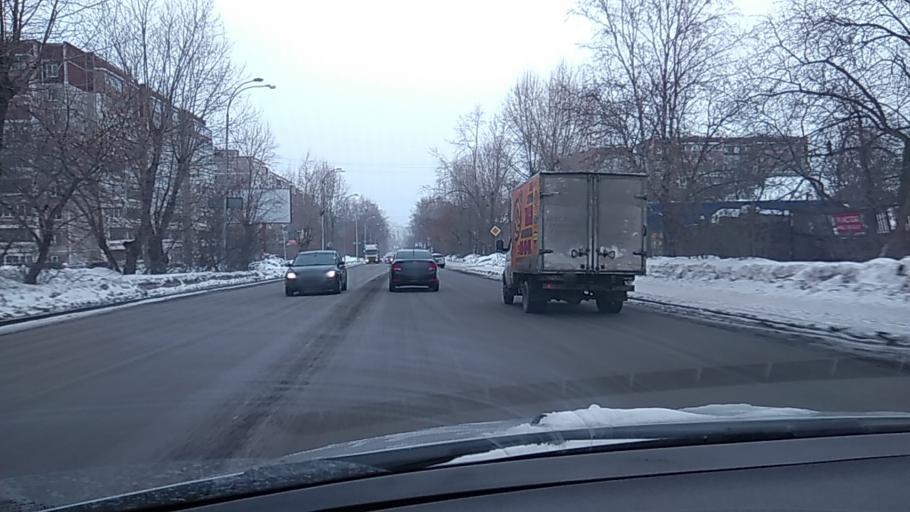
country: RU
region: Sverdlovsk
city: Yekaterinburg
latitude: 56.8980
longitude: 60.6298
